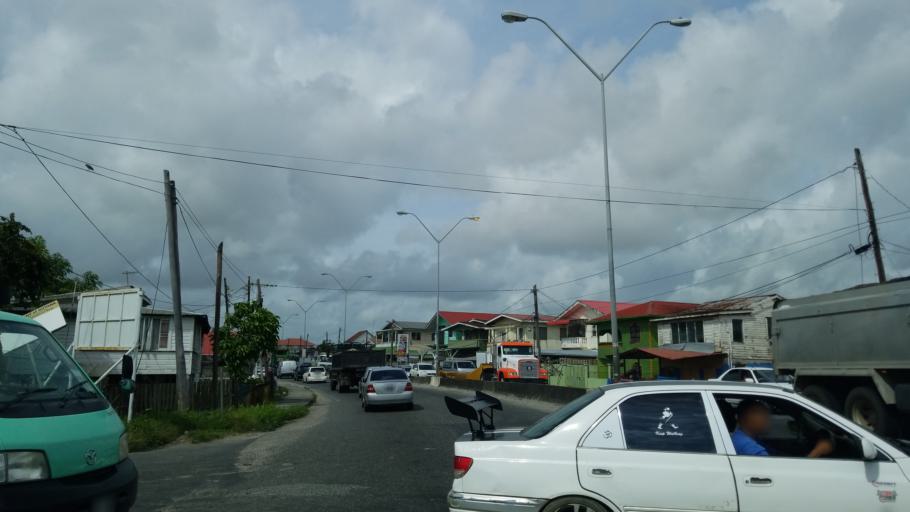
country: GY
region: Demerara-Mahaica
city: Georgetown
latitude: 6.7703
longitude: -58.1758
